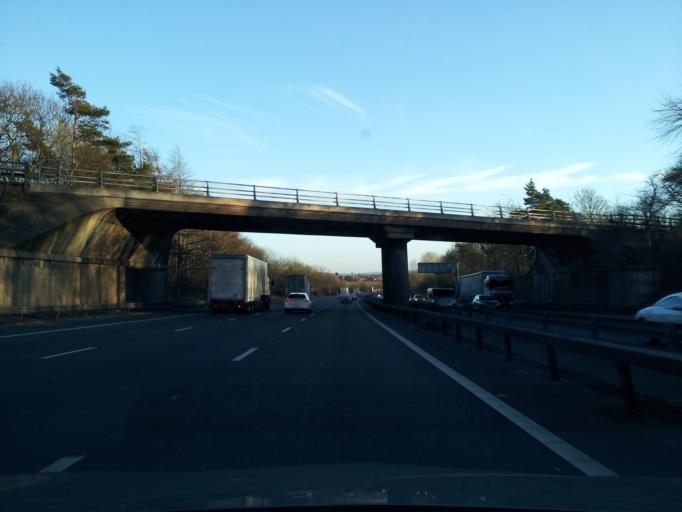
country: GB
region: England
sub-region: Milton Keynes
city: Gayhurst
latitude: 52.0983
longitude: -0.7640
